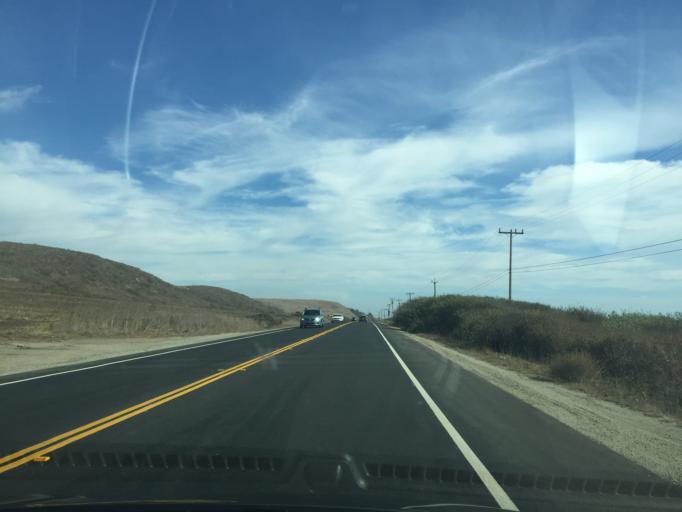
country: US
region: California
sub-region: Santa Cruz County
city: Bonny Doon
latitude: 36.9899
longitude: -122.1618
